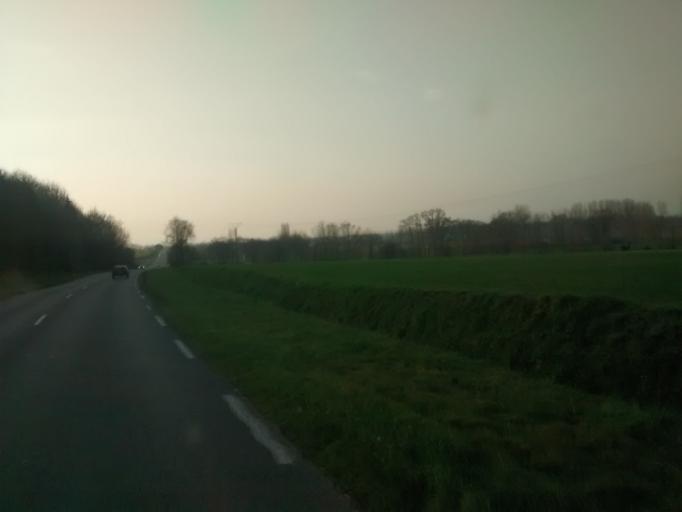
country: FR
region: Brittany
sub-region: Departement d'Ille-et-Vilaine
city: Chavagne
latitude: 48.0594
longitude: -1.8012
